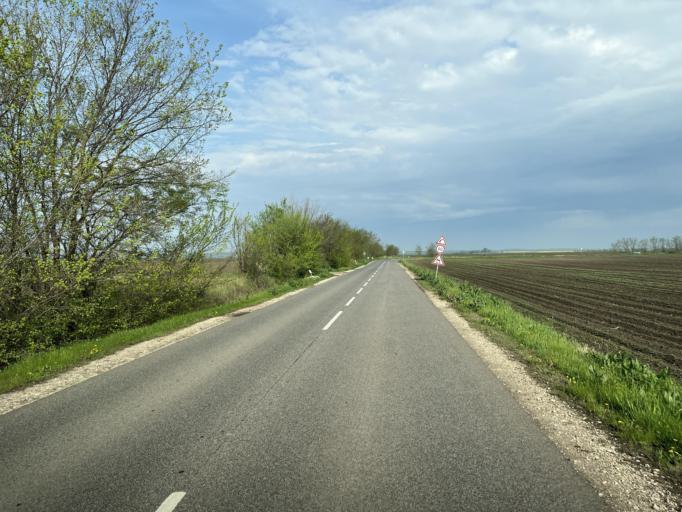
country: HU
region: Pest
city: Tapioszentmarton
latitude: 47.2936
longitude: 19.7517
